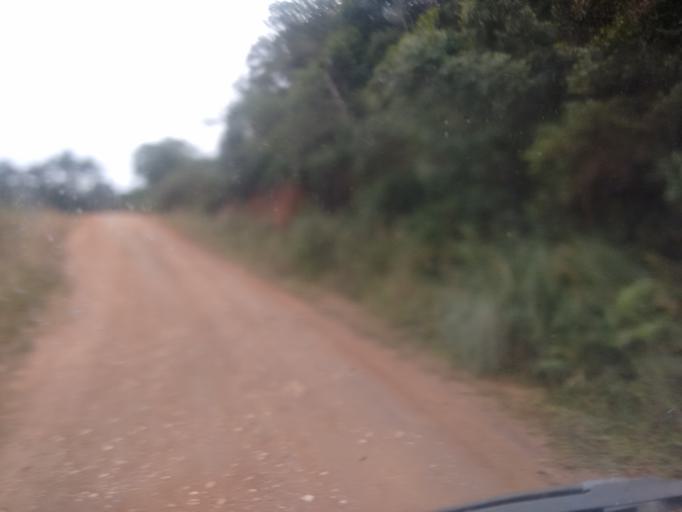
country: BR
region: Rio Grande do Sul
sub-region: Camaqua
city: Camaqua
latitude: -30.7220
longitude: -51.8672
